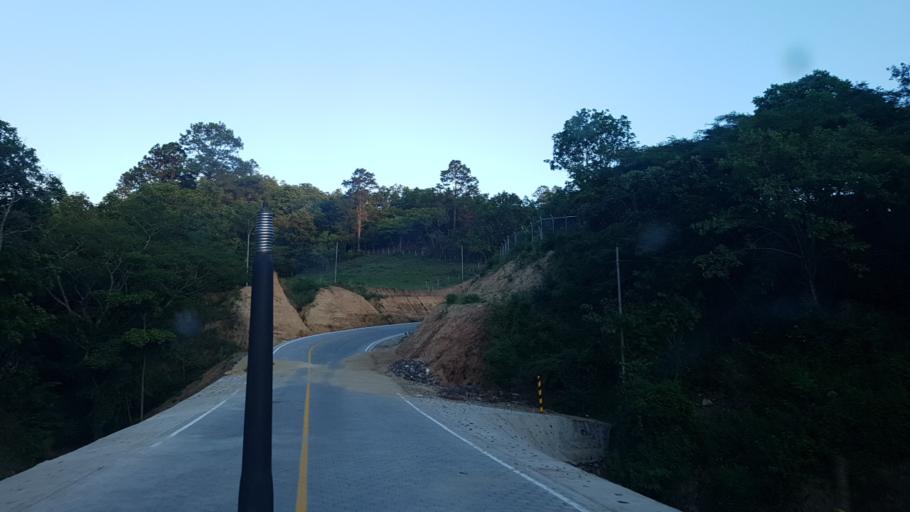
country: NI
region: Nueva Segovia
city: Ocotal
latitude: 13.6808
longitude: -86.6216
